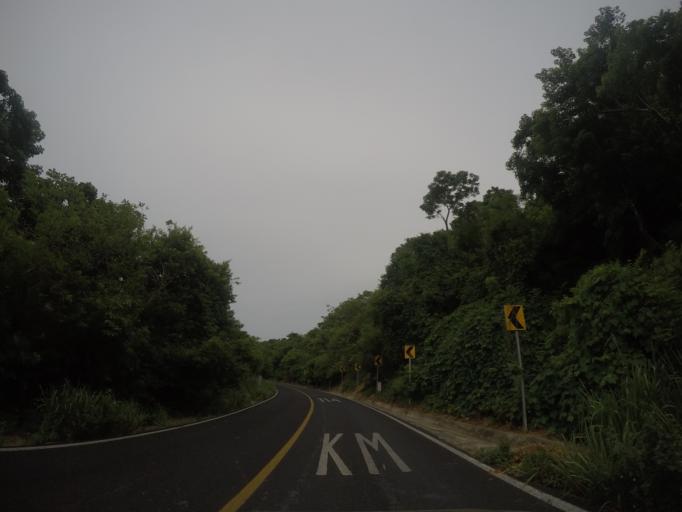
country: MX
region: Oaxaca
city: San Pedro Mixtepec
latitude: 15.9509
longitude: -97.2564
